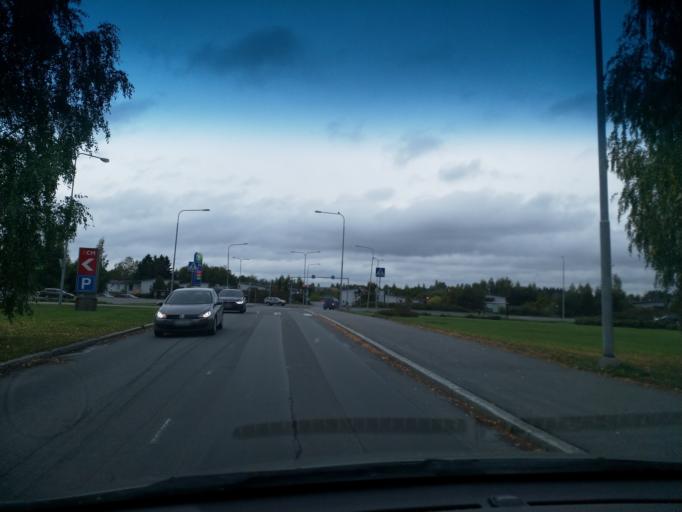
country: FI
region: Pirkanmaa
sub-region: Tampere
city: Tampere
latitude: 61.4775
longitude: 23.8417
